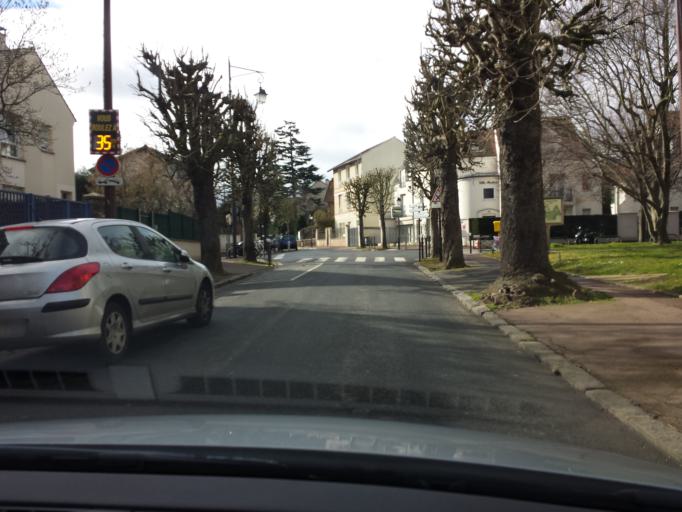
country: FR
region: Ile-de-France
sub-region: Departement des Hauts-de-Seine
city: Antony
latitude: 48.7588
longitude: 2.3004
